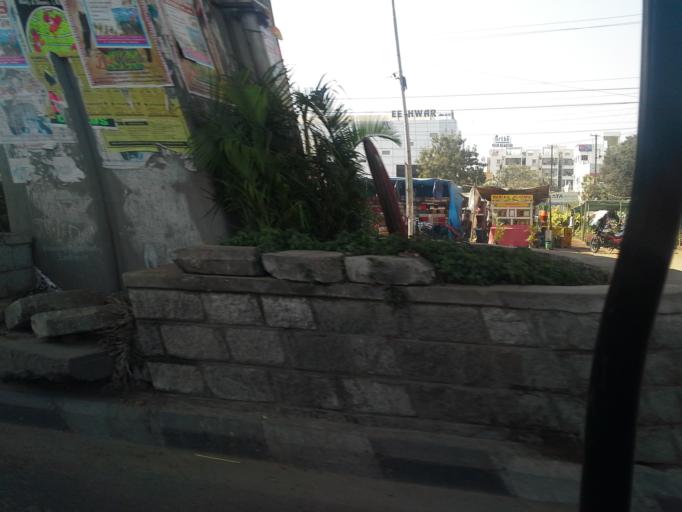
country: IN
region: Telangana
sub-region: Hyderabad
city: Hyderabad
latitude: 17.3666
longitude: 78.4287
